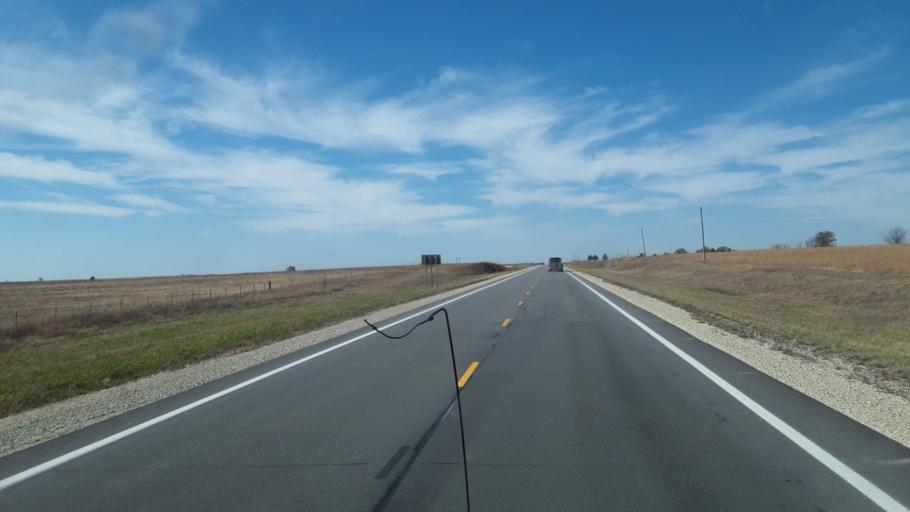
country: US
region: Kansas
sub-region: Marion County
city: Marion
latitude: 38.3630
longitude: -96.8230
